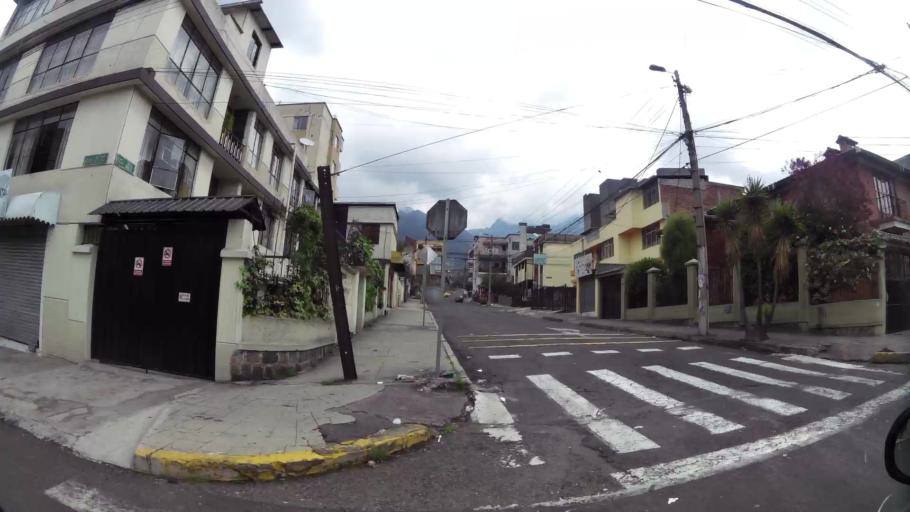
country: EC
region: Pichincha
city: Quito
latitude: -0.1942
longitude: -78.4977
